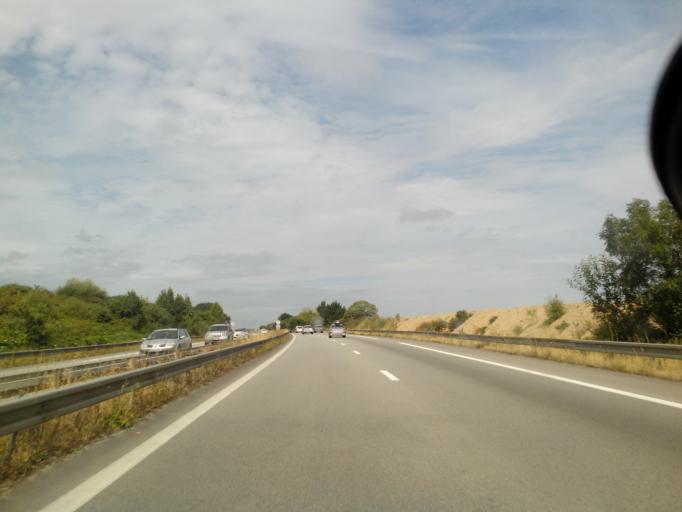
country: FR
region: Brittany
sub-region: Departement du Morbihan
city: Vannes
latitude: 47.6704
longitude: -2.7454
